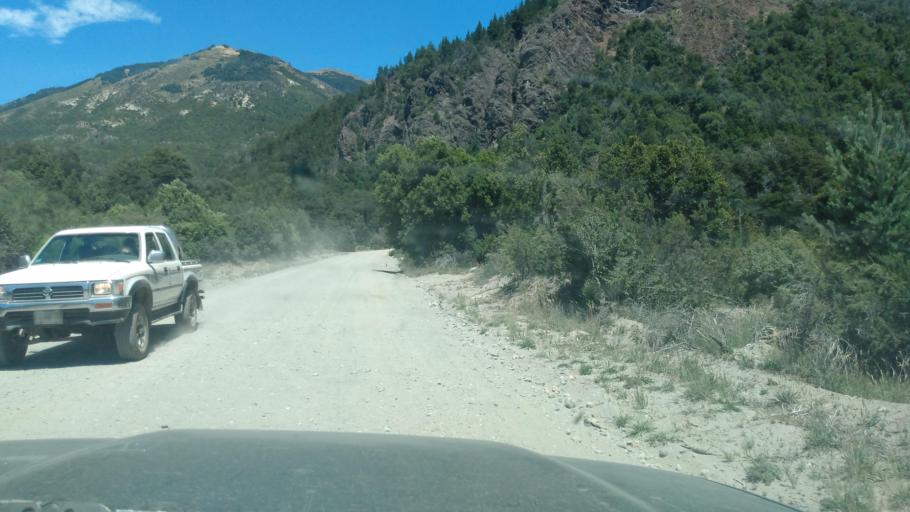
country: AR
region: Rio Negro
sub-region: Departamento de Bariloche
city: San Carlos de Bariloche
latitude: -41.1288
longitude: -71.4506
